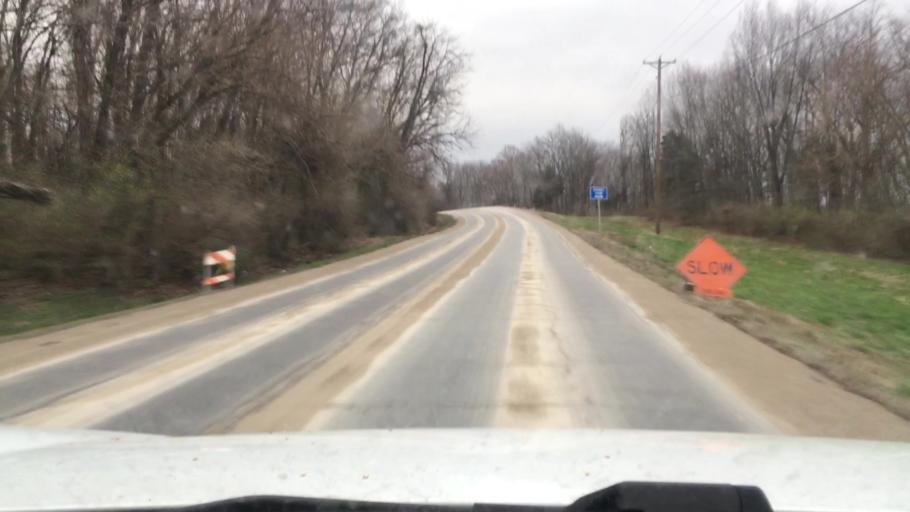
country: US
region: Missouri
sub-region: Saint Charles County
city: Weldon Spring
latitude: 38.6651
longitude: -90.7368
